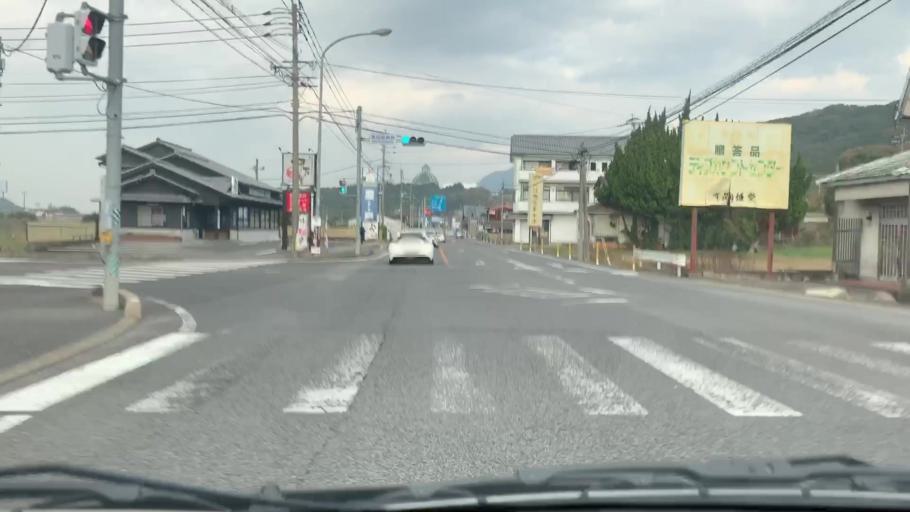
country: JP
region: Saga Prefecture
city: Imaricho-ko
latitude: 33.1810
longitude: 129.8530
